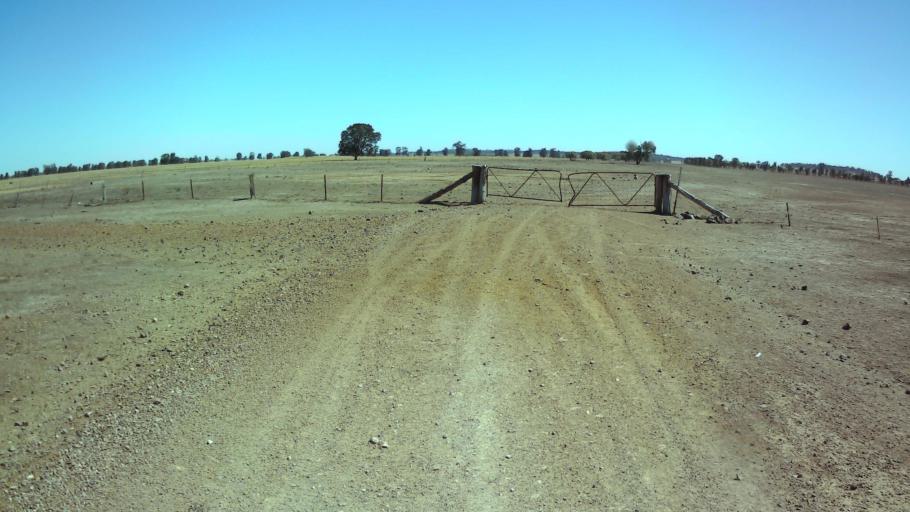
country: AU
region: New South Wales
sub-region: Forbes
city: Forbes
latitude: -33.7248
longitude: 147.6656
